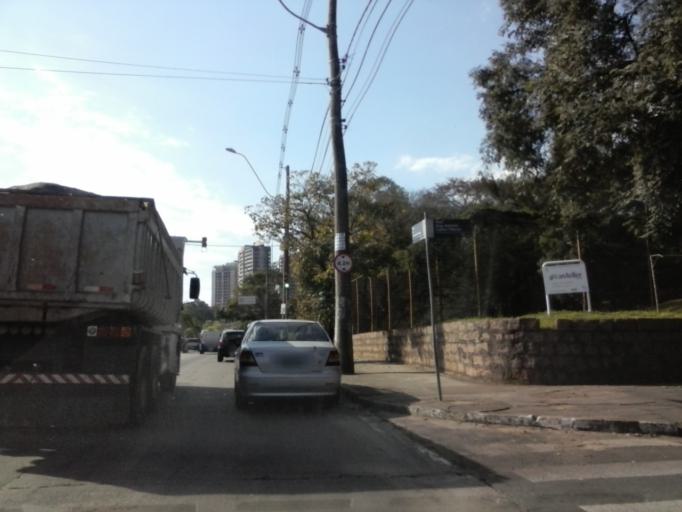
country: BR
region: Rio Grande do Sul
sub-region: Porto Alegre
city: Porto Alegre
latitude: -30.0477
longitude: -51.1784
